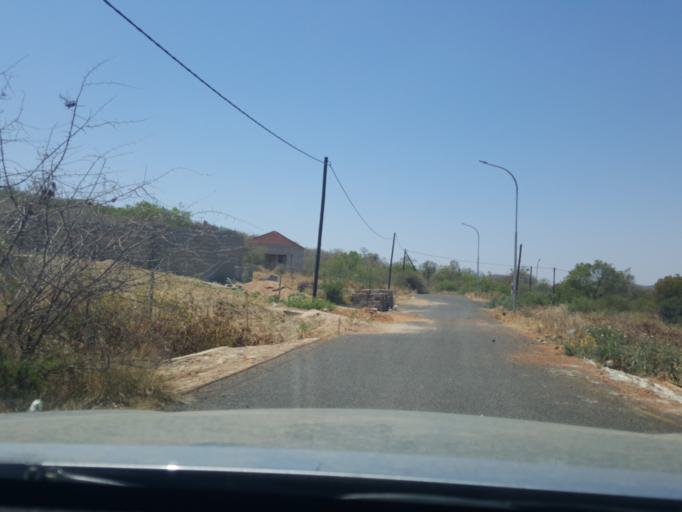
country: BW
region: South East
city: Lobatse
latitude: -25.1866
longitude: 25.6773
